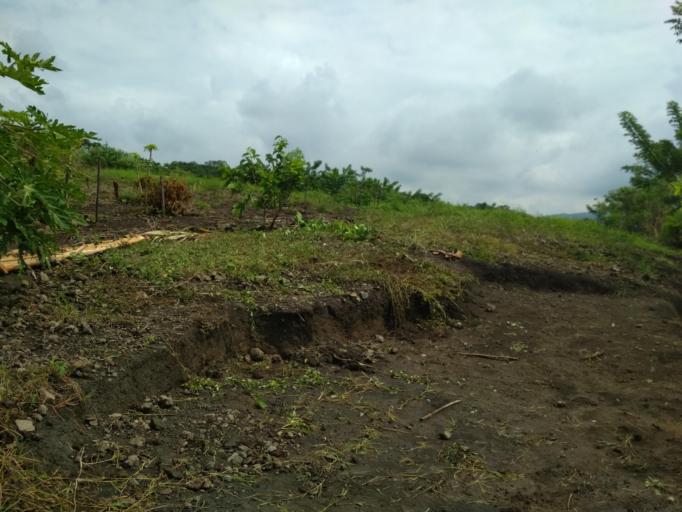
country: MX
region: Veracruz
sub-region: San Andres Tuxtla
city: Cerro las Iguanas
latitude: 18.4176
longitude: -95.1907
